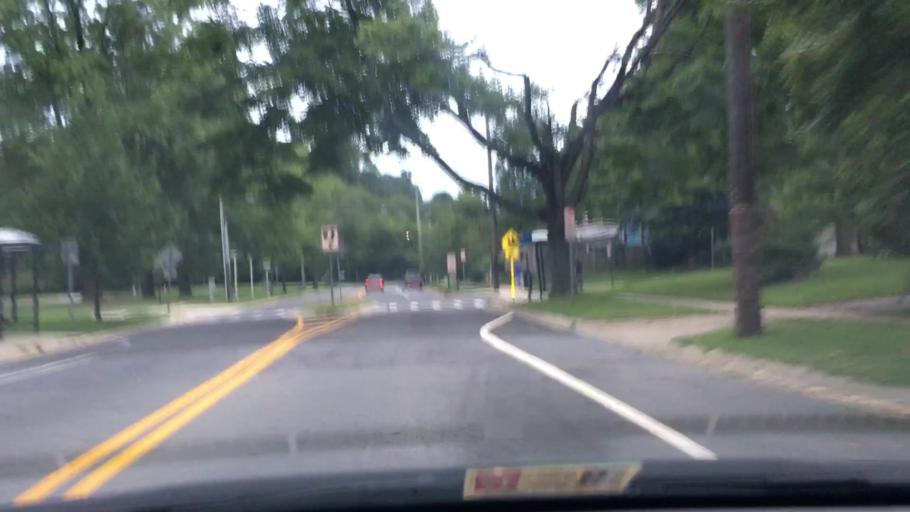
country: US
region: Maryland
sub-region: Montgomery County
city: Rockville
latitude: 39.0824
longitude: -77.1150
